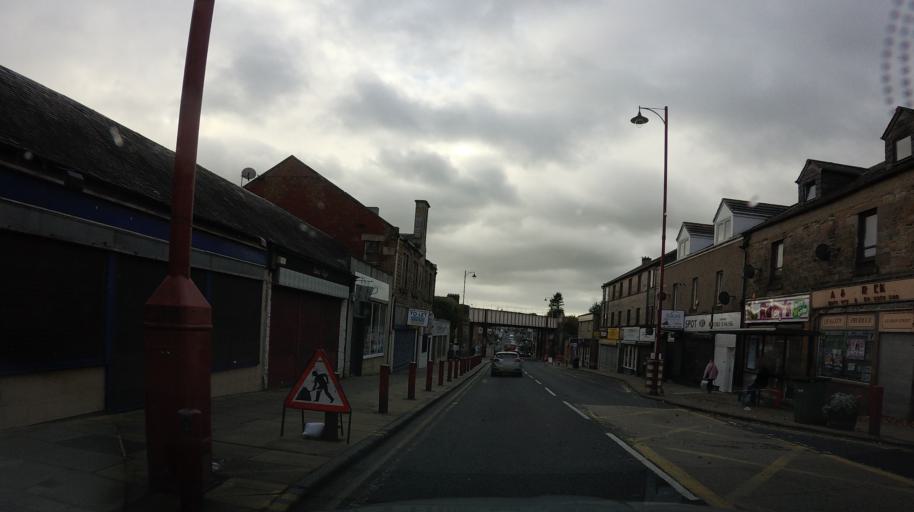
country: GB
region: Scotland
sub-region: Fife
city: Cowdenbeath
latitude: 56.1118
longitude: -3.3440
